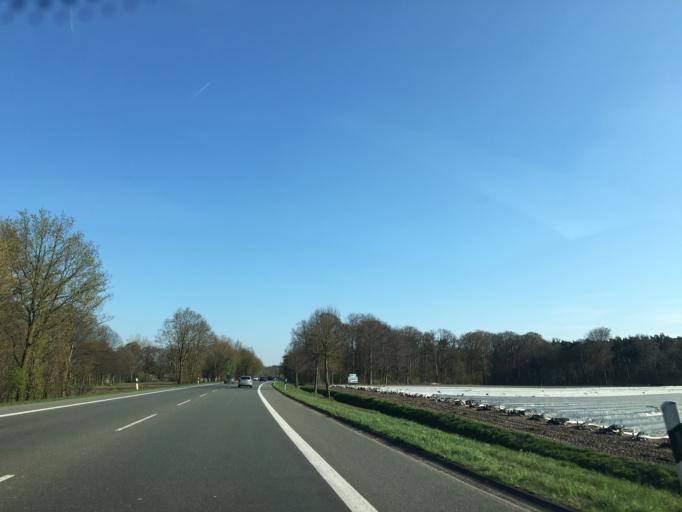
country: DE
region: North Rhine-Westphalia
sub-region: Regierungsbezirk Munster
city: Greven
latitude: 52.0649
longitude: 7.6695
